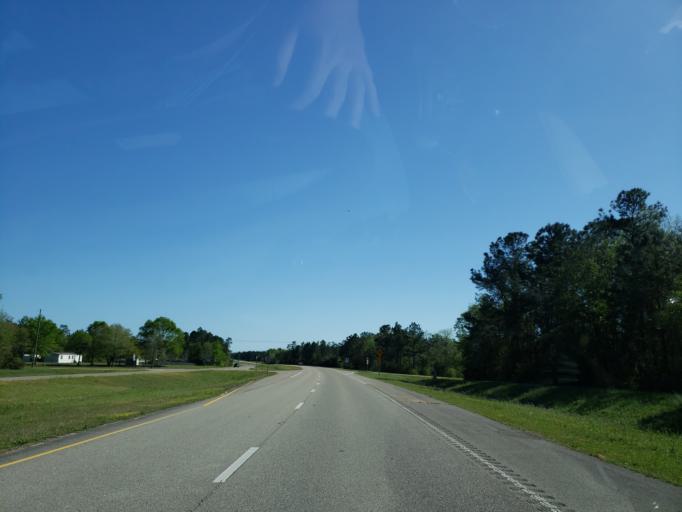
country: US
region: Mississippi
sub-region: Harrison County
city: Lyman
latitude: 30.5198
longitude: -89.0343
